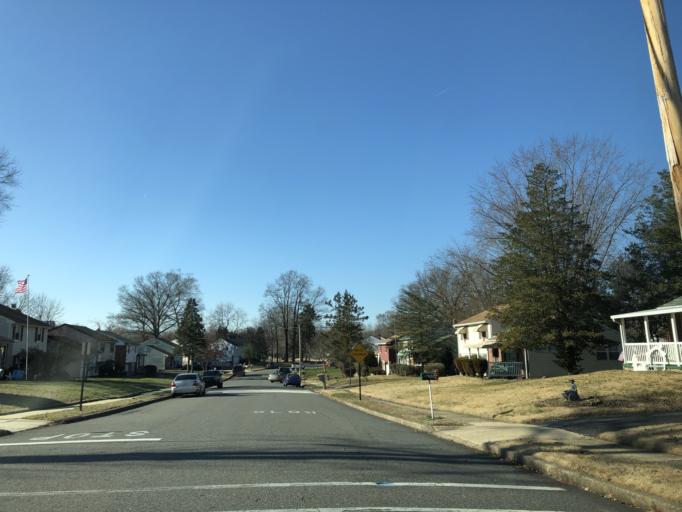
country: US
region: Pennsylvania
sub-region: Delaware County
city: Village Green-Green Ridge
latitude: 39.8484
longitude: -75.4286
